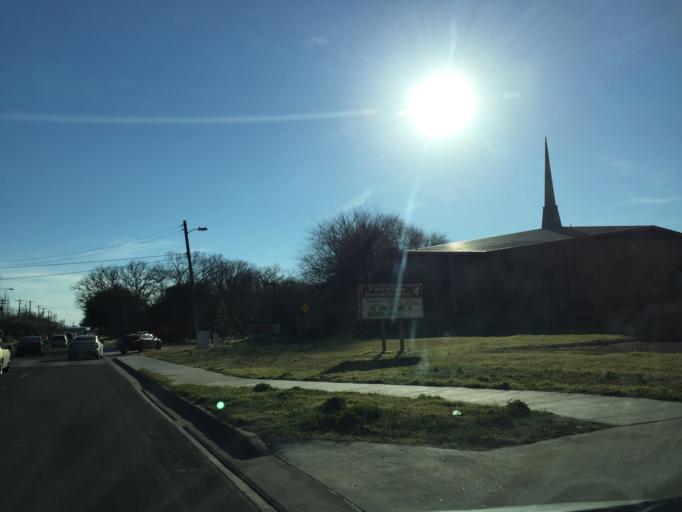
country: US
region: Texas
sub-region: Travis County
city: Rollingwood
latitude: 30.2073
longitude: -97.7822
